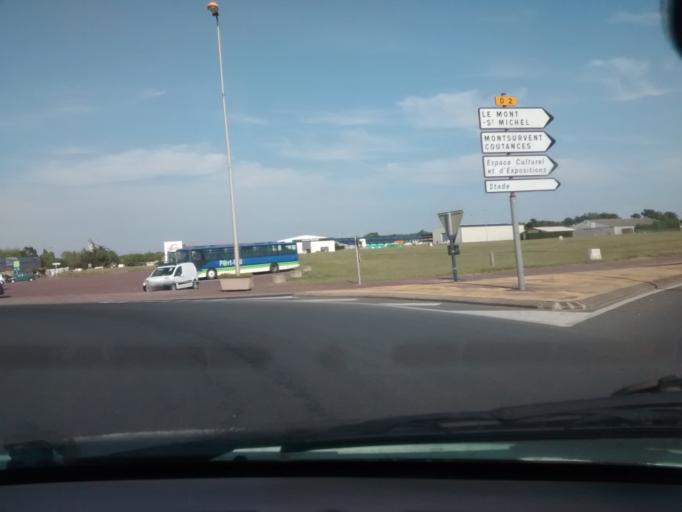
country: FR
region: Lower Normandy
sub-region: Departement de la Manche
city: Lessay
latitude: 49.2120
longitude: -1.5285
